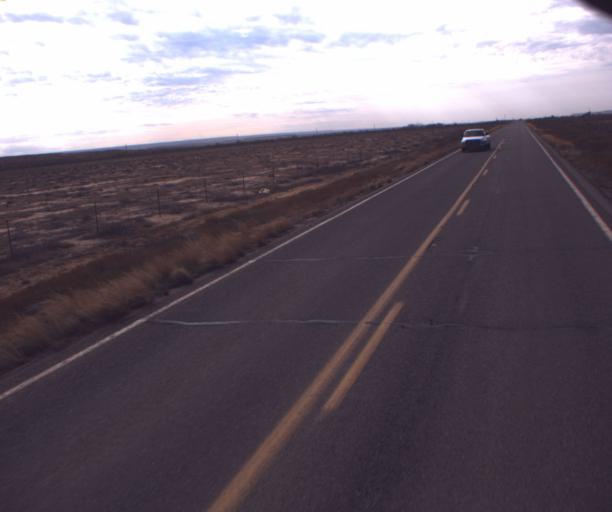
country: US
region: Arizona
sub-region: Apache County
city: Many Farms
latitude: 36.4523
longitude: -109.6079
